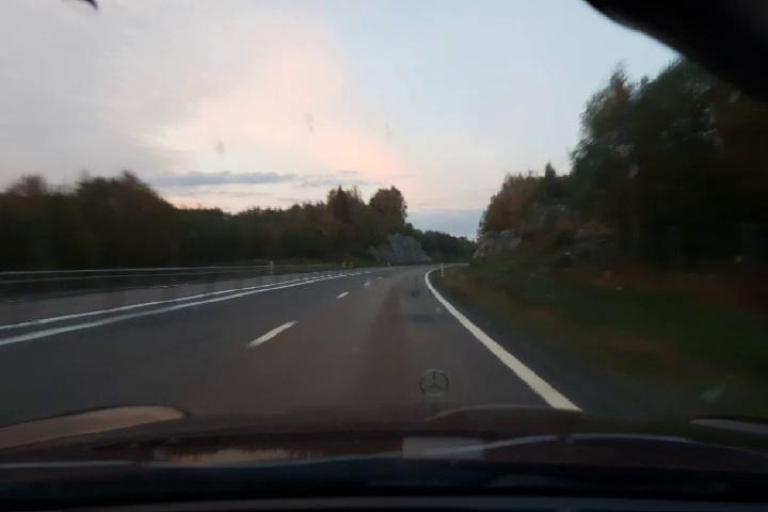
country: SE
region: Vaesternorrland
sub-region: Haernoesands Kommun
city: Haernoesand
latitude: 62.8399
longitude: 17.9745
